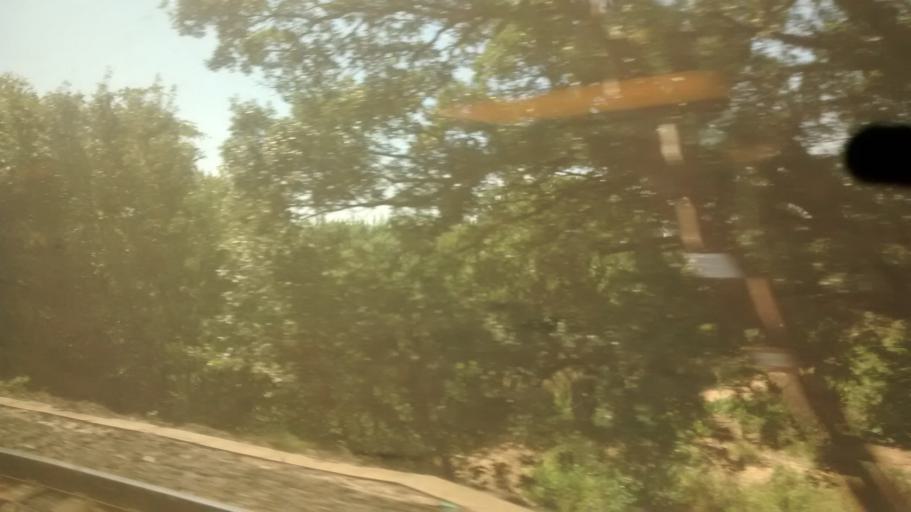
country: FR
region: Languedoc-Roussillon
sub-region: Departement de l'Herault
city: Saint-Aunes
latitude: 43.6432
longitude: 3.9822
